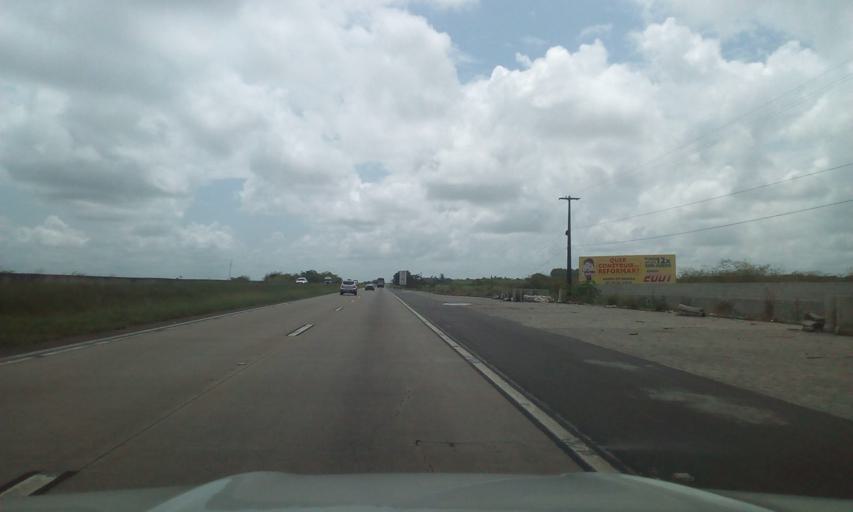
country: BR
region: Pernambuco
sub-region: Goiana
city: Goiana
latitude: -7.6559
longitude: -34.9417
